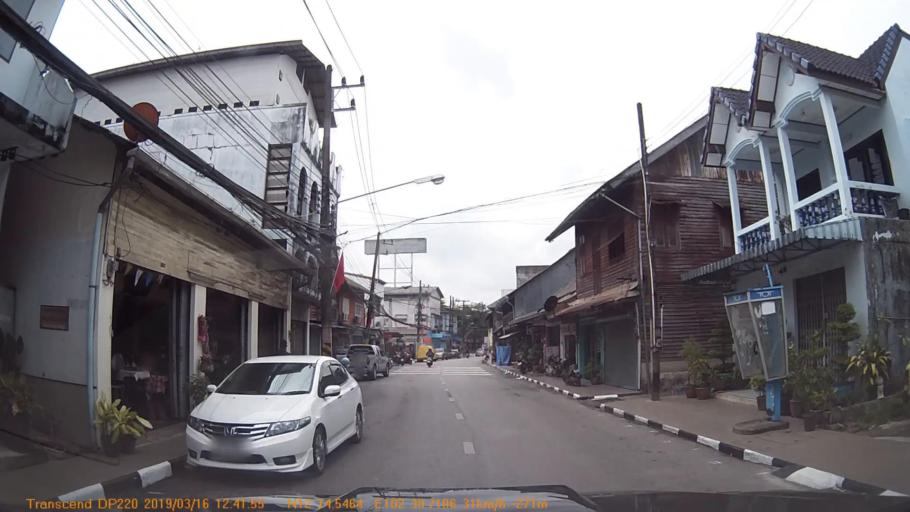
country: TH
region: Trat
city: Trat
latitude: 12.2425
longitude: 102.5117
